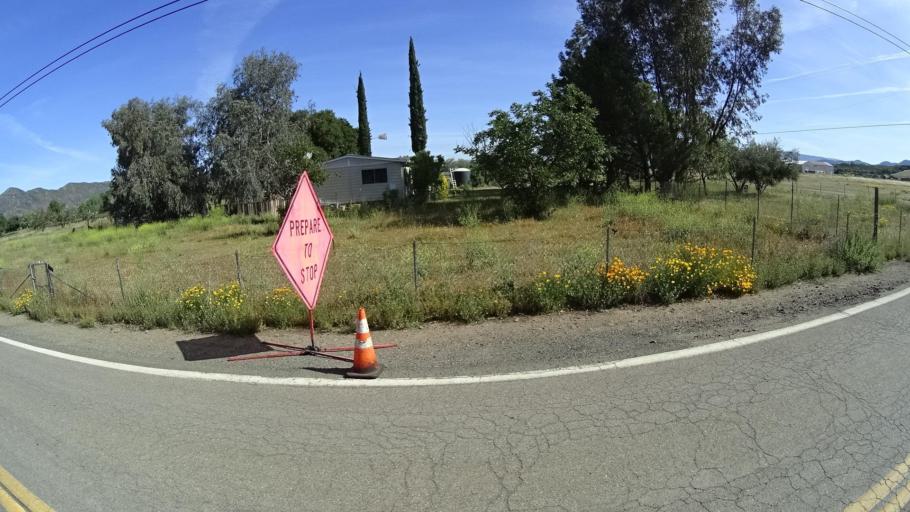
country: US
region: California
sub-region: Lake County
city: Kelseyville
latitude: 38.9573
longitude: -122.8863
